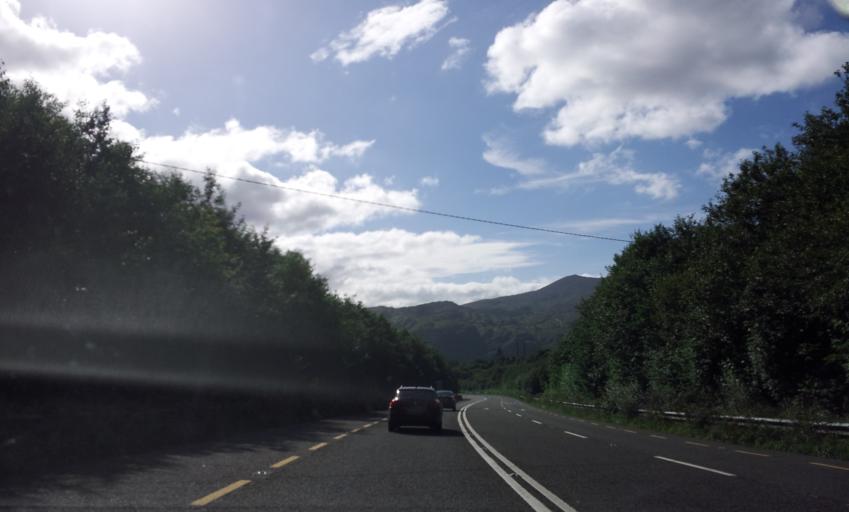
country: IE
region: Munster
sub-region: Ciarrai
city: Cill Airne
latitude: 51.9824
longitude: -9.3064
